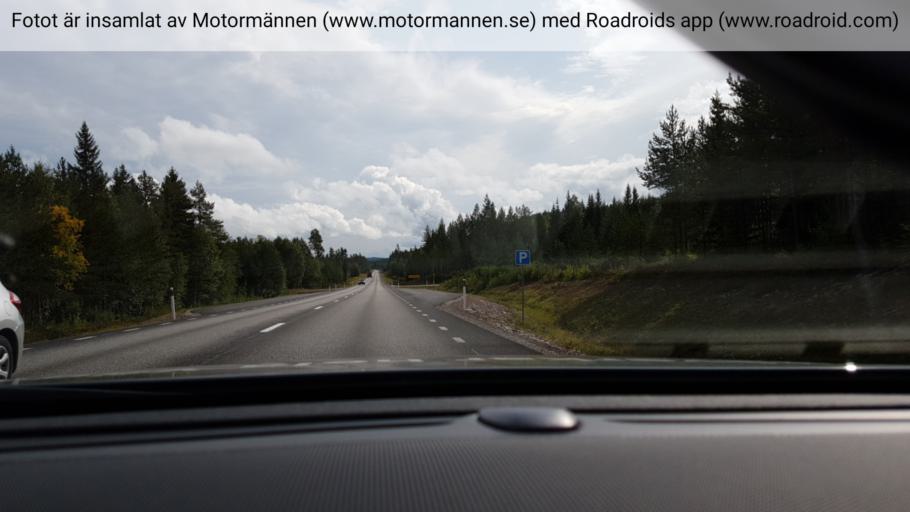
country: SE
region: Dalarna
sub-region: Rattviks Kommun
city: Raettvik
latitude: 60.8176
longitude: 15.2584
